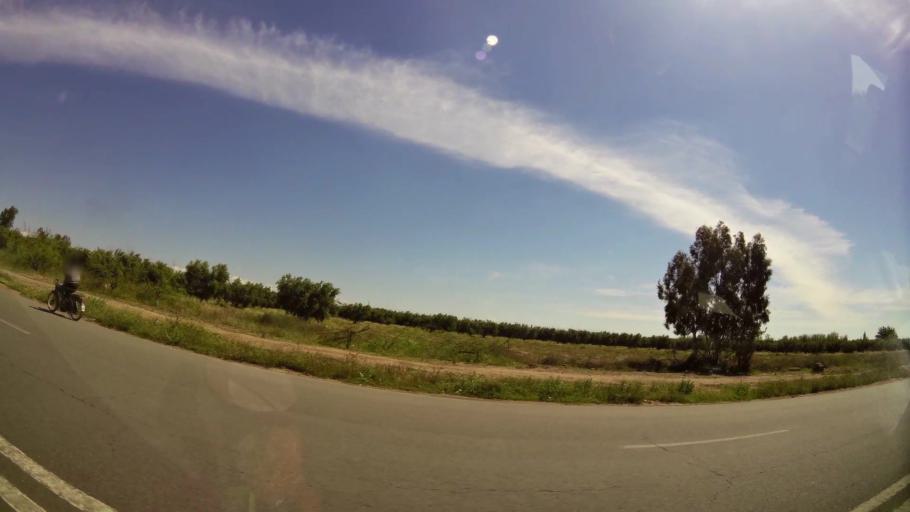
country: MA
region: Marrakech-Tensift-Al Haouz
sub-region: Marrakech
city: Marrakesh
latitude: 31.6395
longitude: -8.0854
